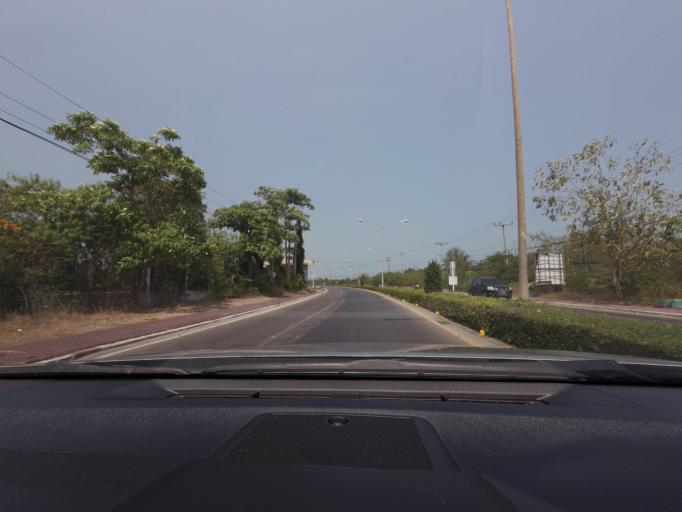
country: TH
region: Phetchaburi
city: Cha-am
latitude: 12.8123
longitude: 99.9806
